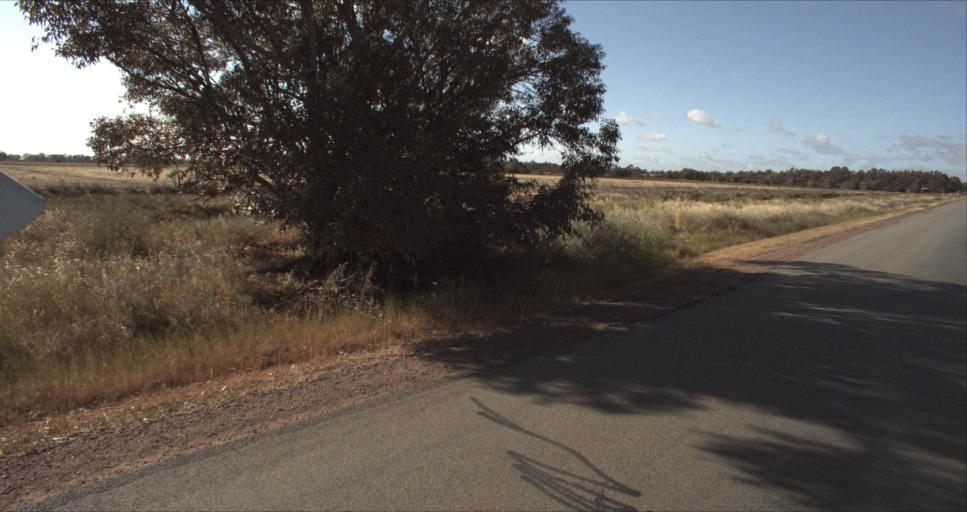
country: AU
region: New South Wales
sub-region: Leeton
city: Leeton
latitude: -34.5232
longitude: 146.3902
